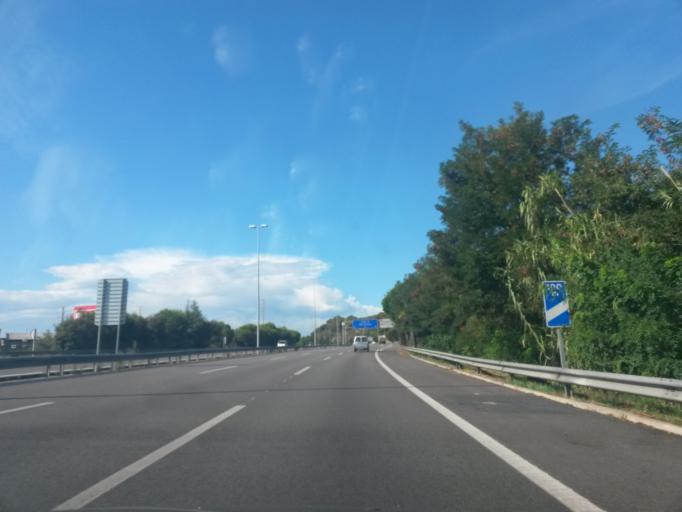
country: ES
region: Catalonia
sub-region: Provincia de Barcelona
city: Cabrera de Mar
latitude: 41.5327
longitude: 2.4157
